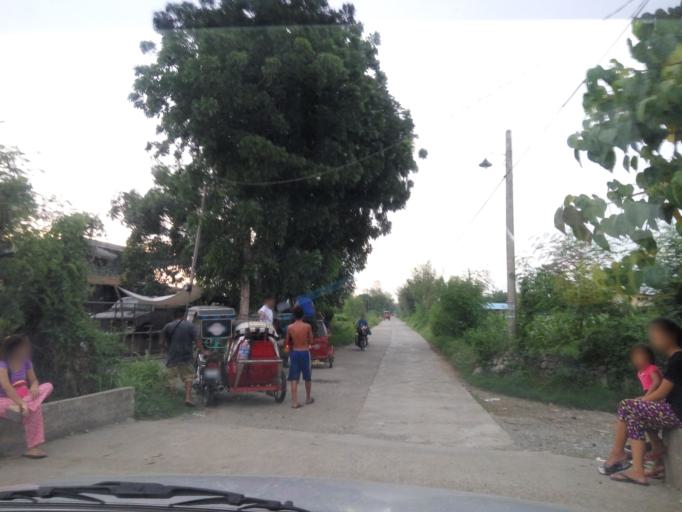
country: PH
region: Ilocos
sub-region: Province of La Union
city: Rosario
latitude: 16.2081
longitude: 120.4706
